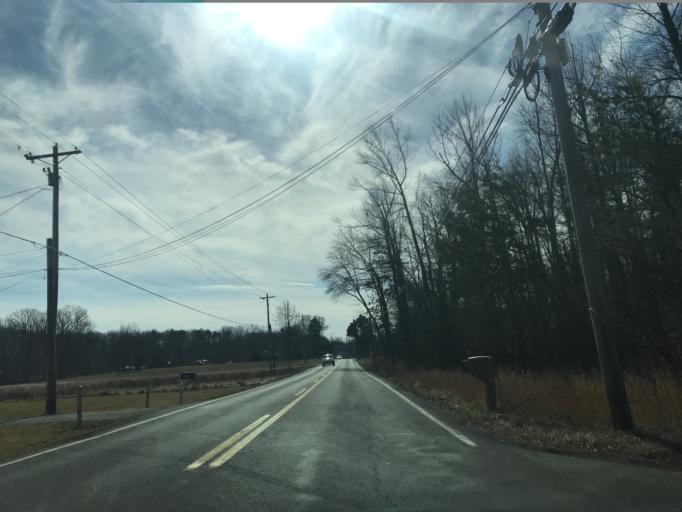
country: US
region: Maryland
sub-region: Charles County
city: Potomac Heights
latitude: 38.5531
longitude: -77.1292
